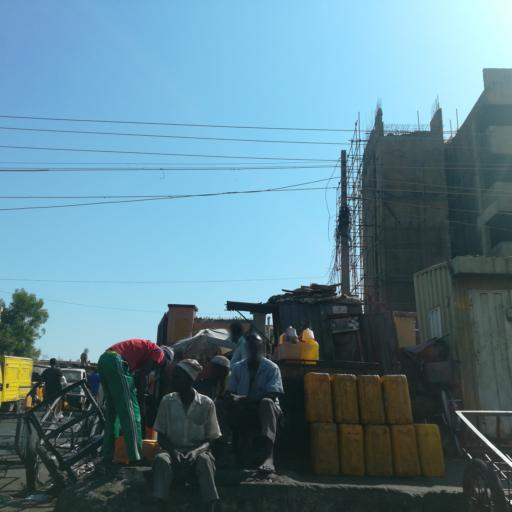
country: NG
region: Kano
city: Kano
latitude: 12.0118
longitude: 8.5327
